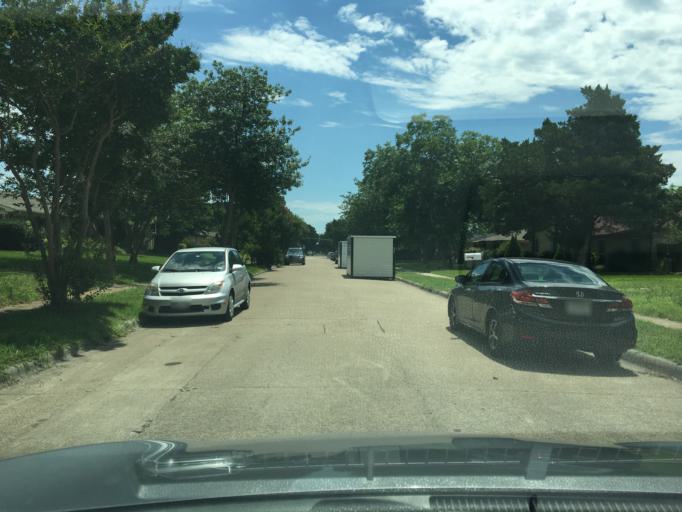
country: US
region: Texas
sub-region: Dallas County
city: Richardson
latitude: 32.9336
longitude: -96.6929
